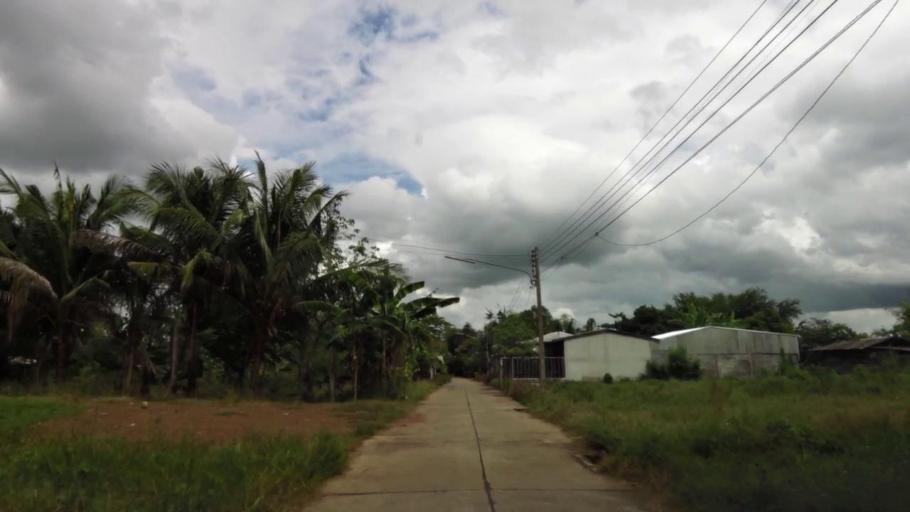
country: TH
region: Nakhon Sawan
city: Phai Sali
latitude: 15.5999
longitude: 100.6534
